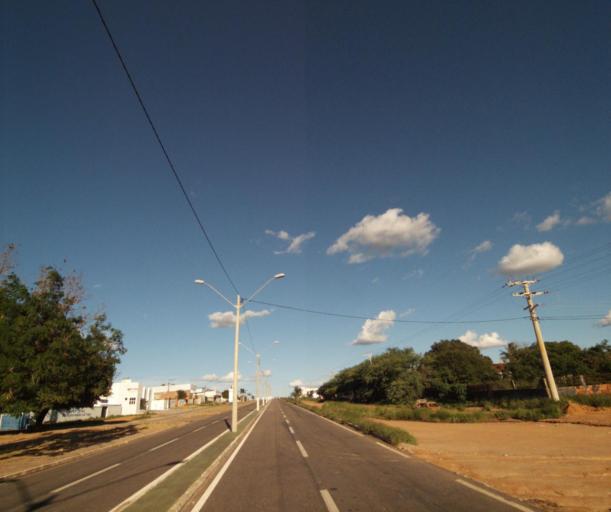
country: BR
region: Bahia
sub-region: Guanambi
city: Guanambi
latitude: -14.2094
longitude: -42.7724
